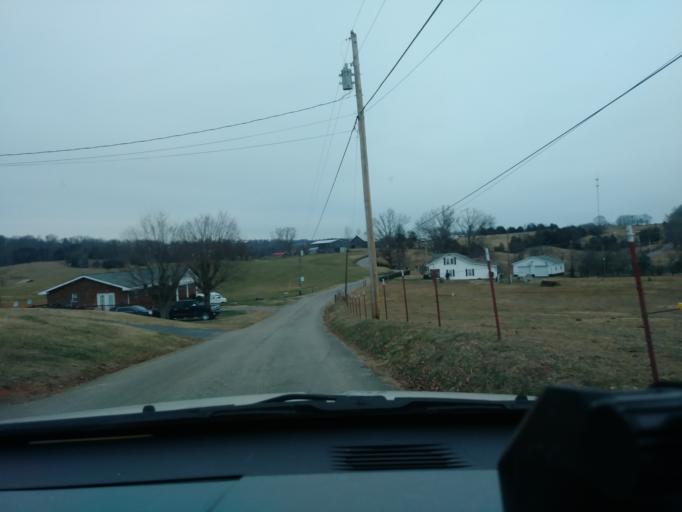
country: US
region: Tennessee
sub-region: Greene County
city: Greeneville
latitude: 36.0994
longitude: -82.8902
